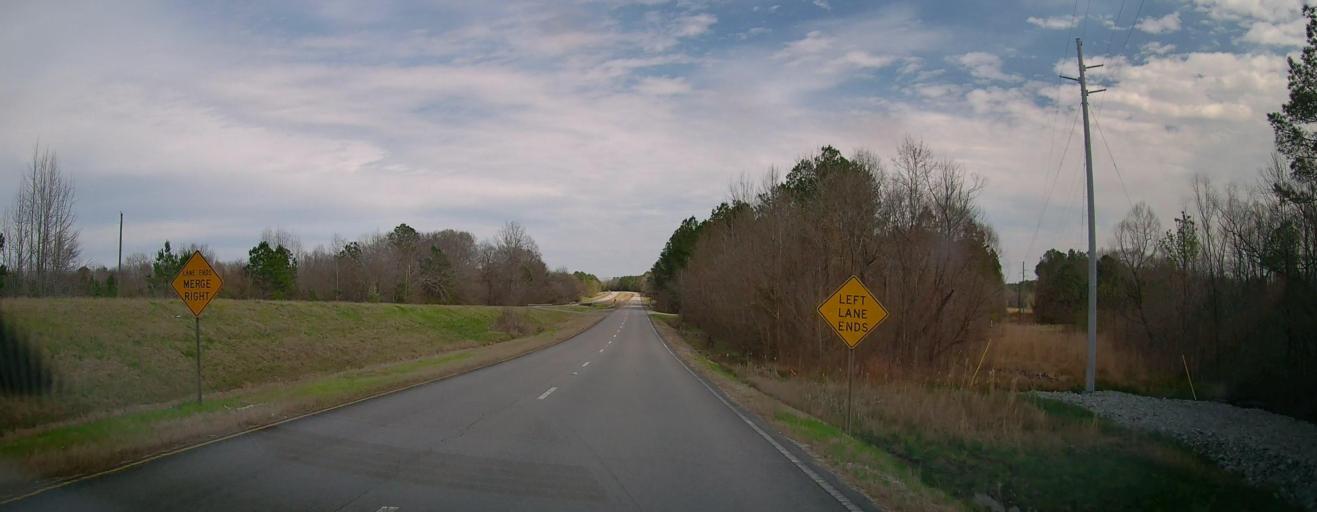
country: US
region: Alabama
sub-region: Marion County
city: Winfield
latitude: 33.9300
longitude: -87.6833
